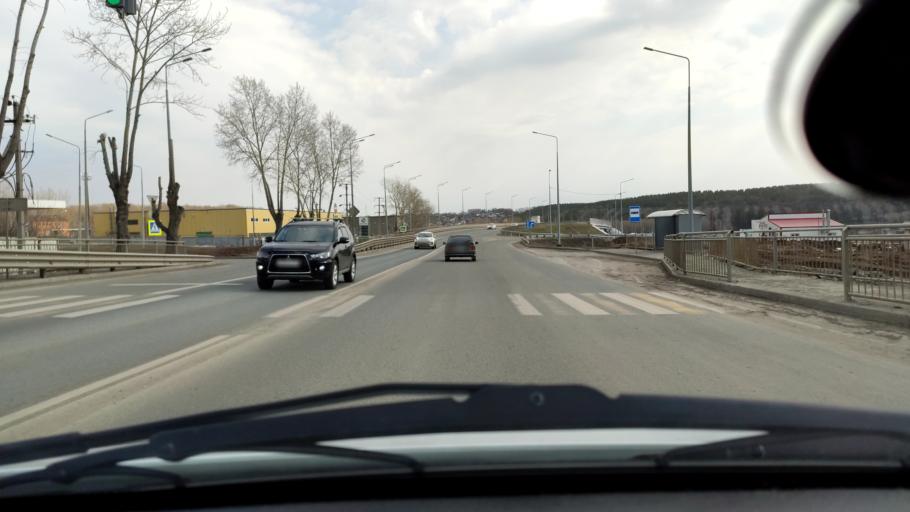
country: RU
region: Bashkortostan
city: Ufa
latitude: 54.8301
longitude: 56.1205
